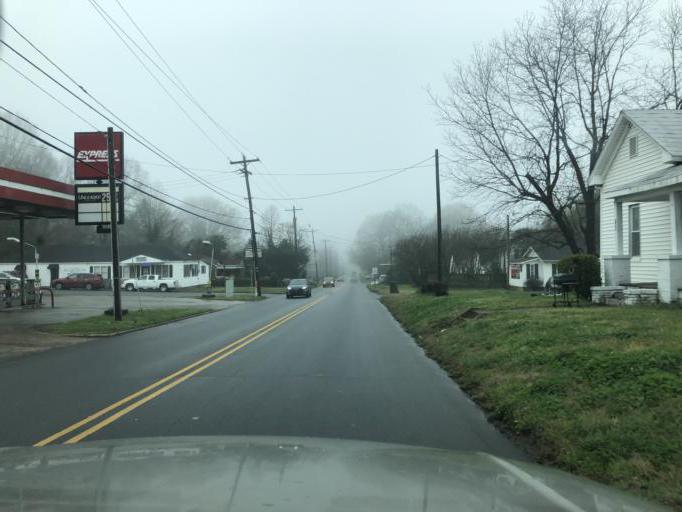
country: US
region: North Carolina
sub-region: Gaston County
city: Cherryville
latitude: 35.3795
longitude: -81.3886
